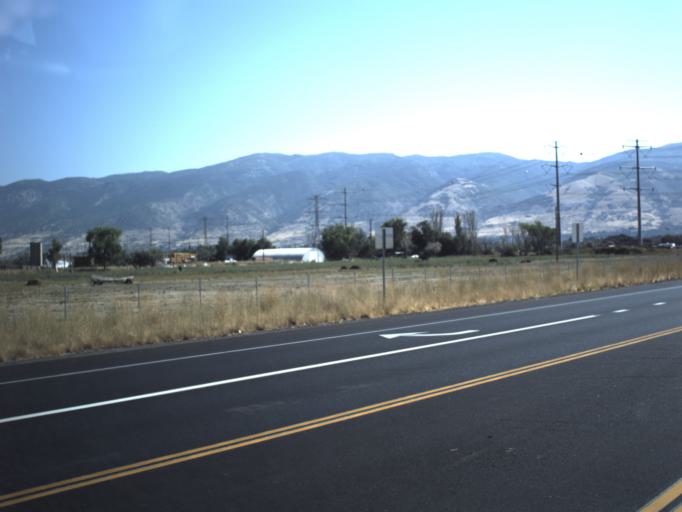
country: US
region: Utah
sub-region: Davis County
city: West Bountiful
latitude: 40.8840
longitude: -111.9339
